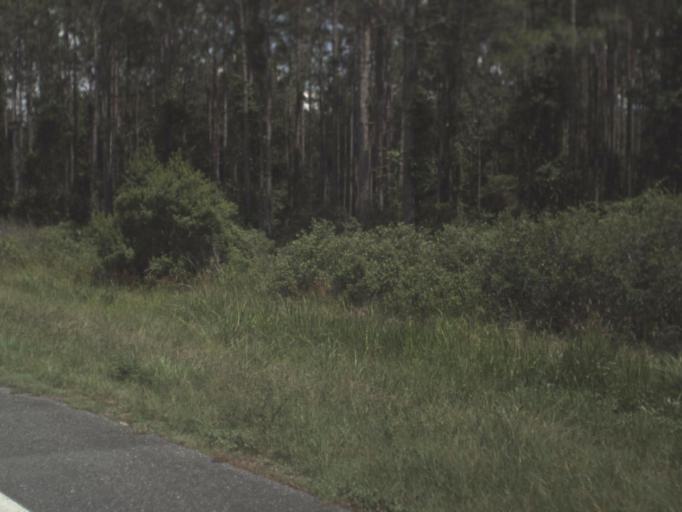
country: US
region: Florida
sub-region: Gilchrist County
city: Trenton
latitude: 29.6229
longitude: -82.7520
